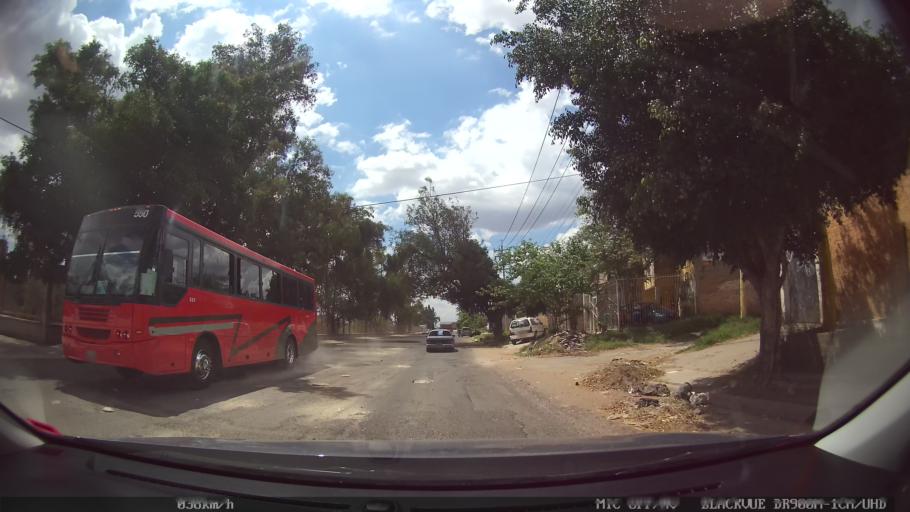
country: MX
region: Jalisco
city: Tlaquepaque
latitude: 20.6747
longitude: -103.2648
